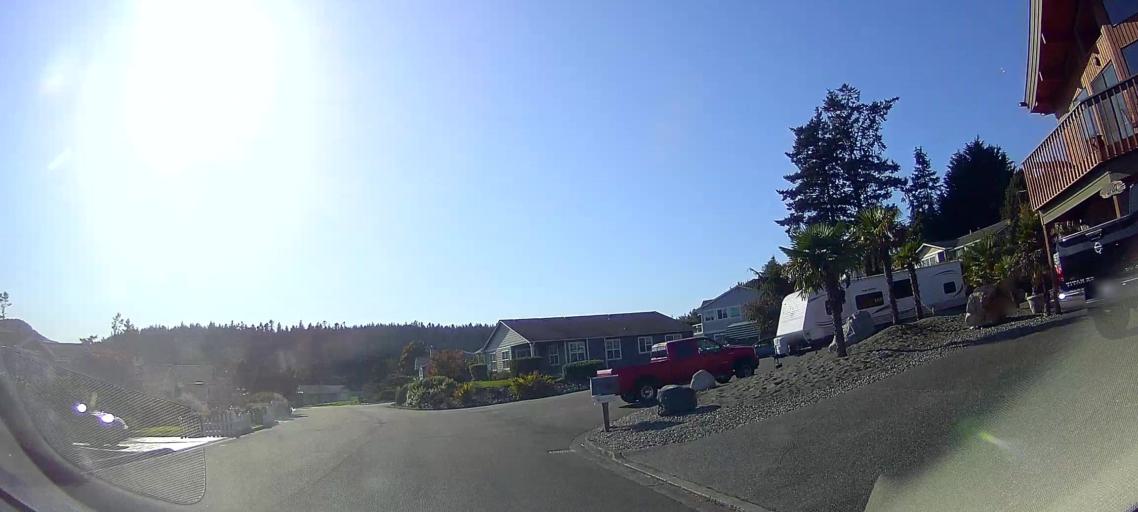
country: US
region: Washington
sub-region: Skagit County
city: Anacortes
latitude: 48.4982
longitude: -122.6828
